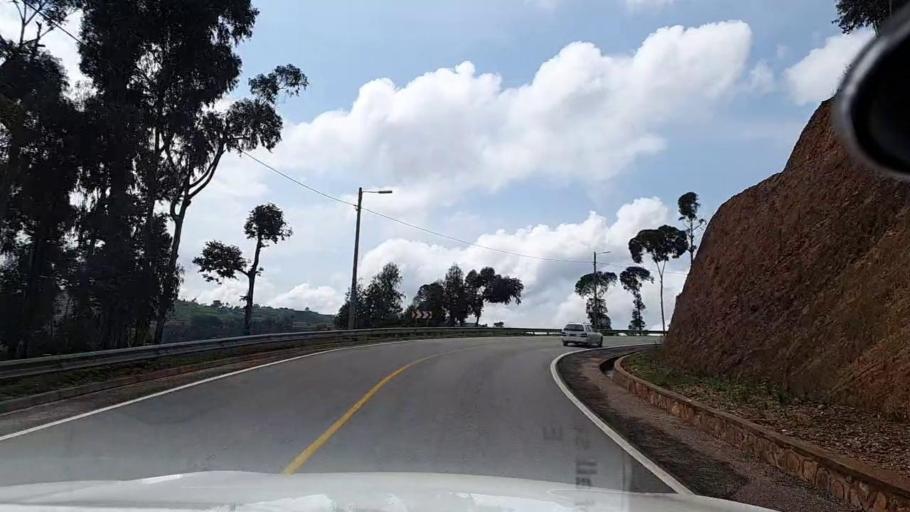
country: RW
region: Southern Province
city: Nzega
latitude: -2.5121
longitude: 29.4640
